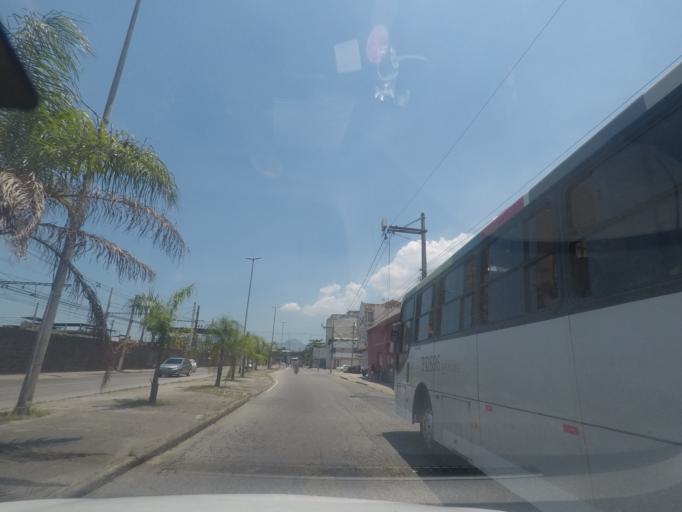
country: BR
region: Rio de Janeiro
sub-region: Duque De Caxias
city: Duque de Caxias
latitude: -22.8122
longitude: -43.3014
